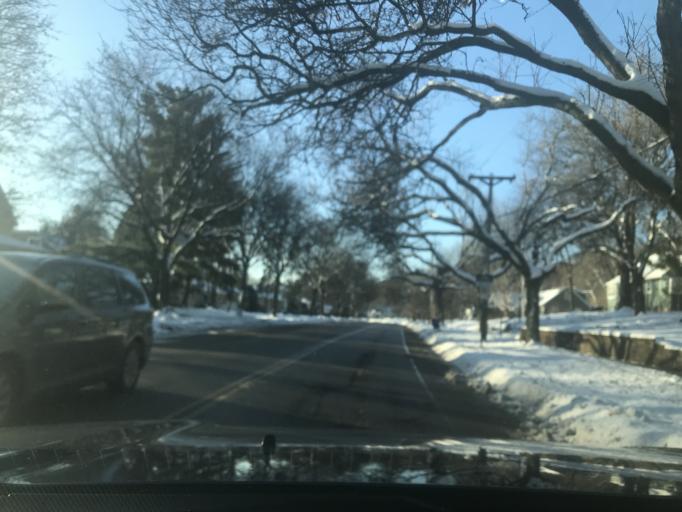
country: US
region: Minnesota
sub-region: Dakota County
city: Mendota Heights
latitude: 44.9195
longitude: -93.1468
